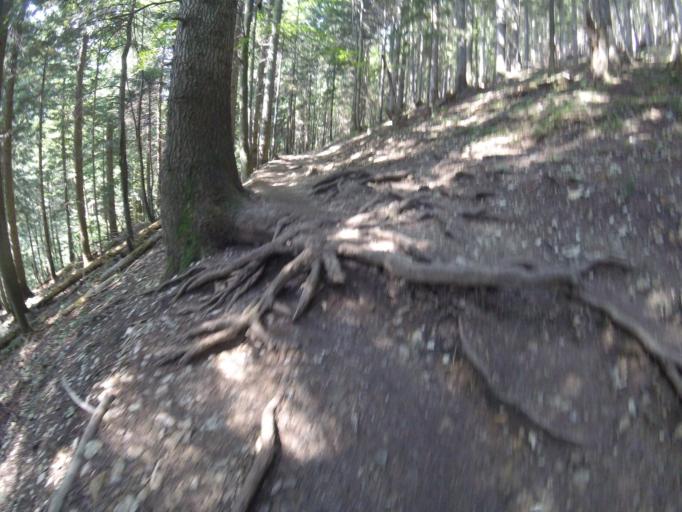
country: SK
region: Zilinsky
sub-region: Okres Zilina
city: Terchova
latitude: 49.2438
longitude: 19.0742
